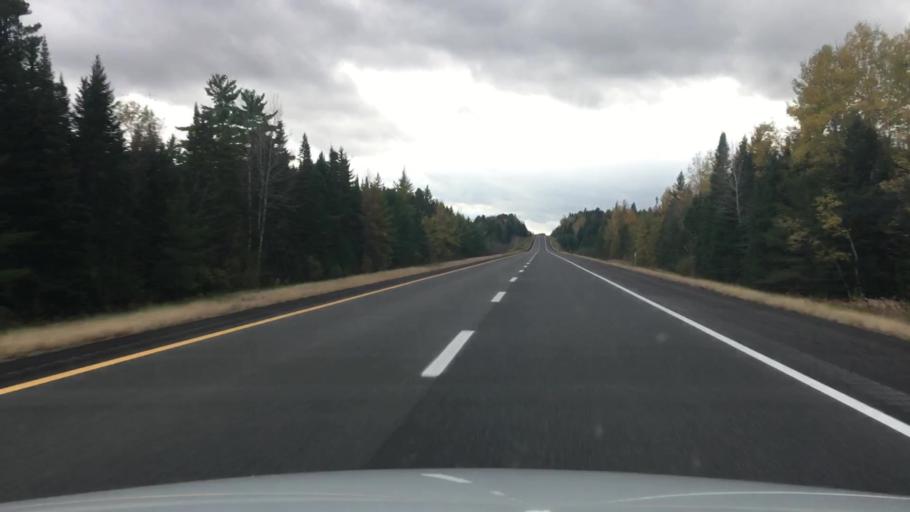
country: US
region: Maine
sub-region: Penobscot County
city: Patten
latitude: 46.0680
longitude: -68.2267
